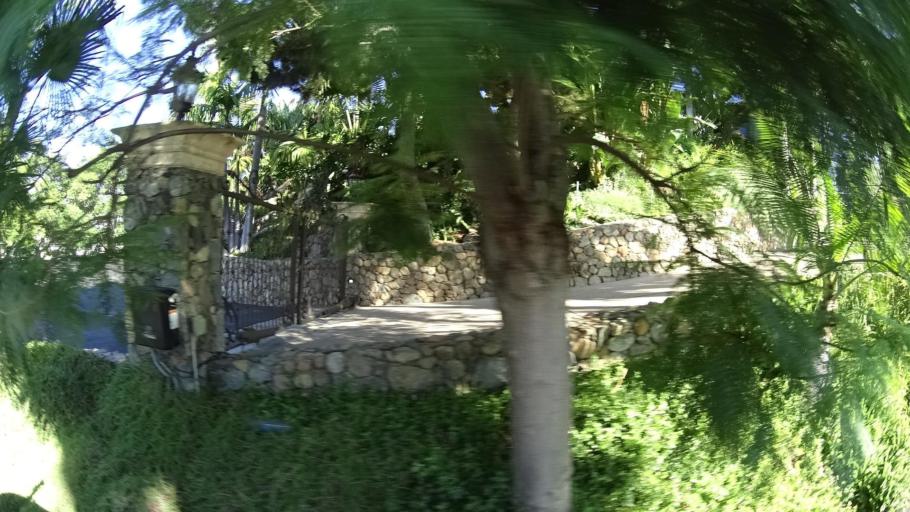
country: US
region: California
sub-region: San Diego County
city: Casa de Oro-Mount Helix
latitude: 32.7664
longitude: -116.9868
